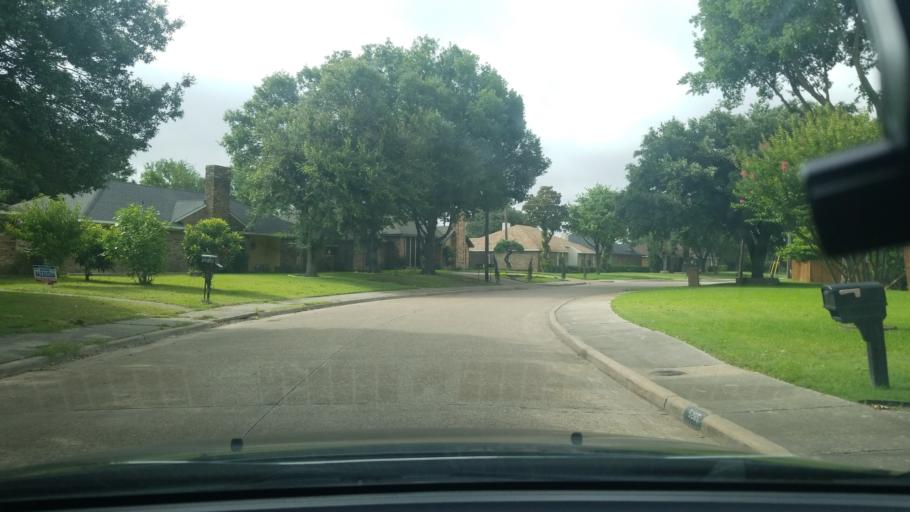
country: US
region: Texas
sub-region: Dallas County
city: Balch Springs
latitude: 32.7903
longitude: -96.6870
